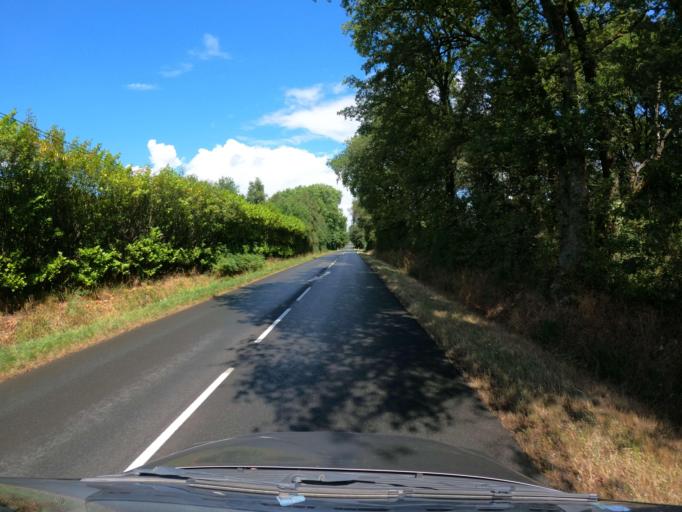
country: FR
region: Pays de la Loire
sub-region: Departement de Maine-et-Loire
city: Champigne
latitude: 47.6313
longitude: -0.5807
